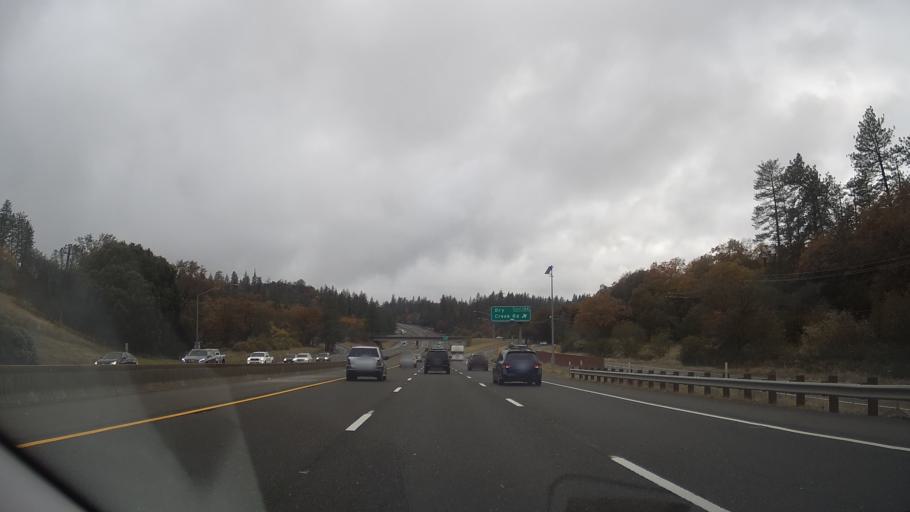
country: US
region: California
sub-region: Placer County
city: Meadow Vista
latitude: 38.9603
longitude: -121.0289
